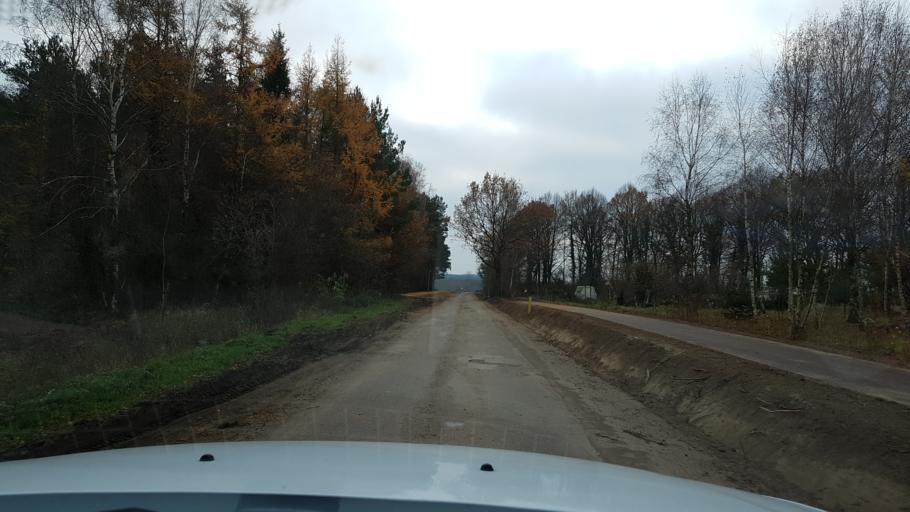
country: PL
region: West Pomeranian Voivodeship
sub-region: Powiat kolobrzeski
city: Grzybowo
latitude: 54.1137
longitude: 15.5244
